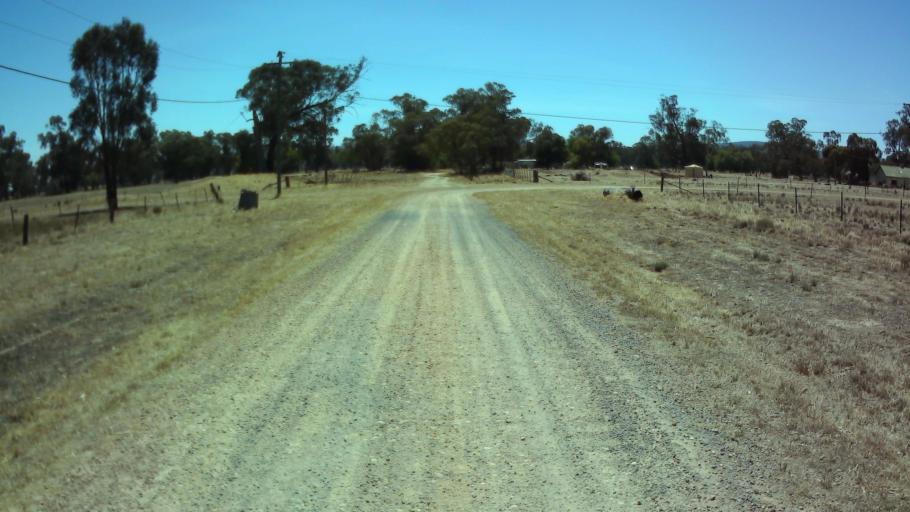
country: AU
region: New South Wales
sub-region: Weddin
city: Grenfell
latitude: -34.0375
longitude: 147.9271
